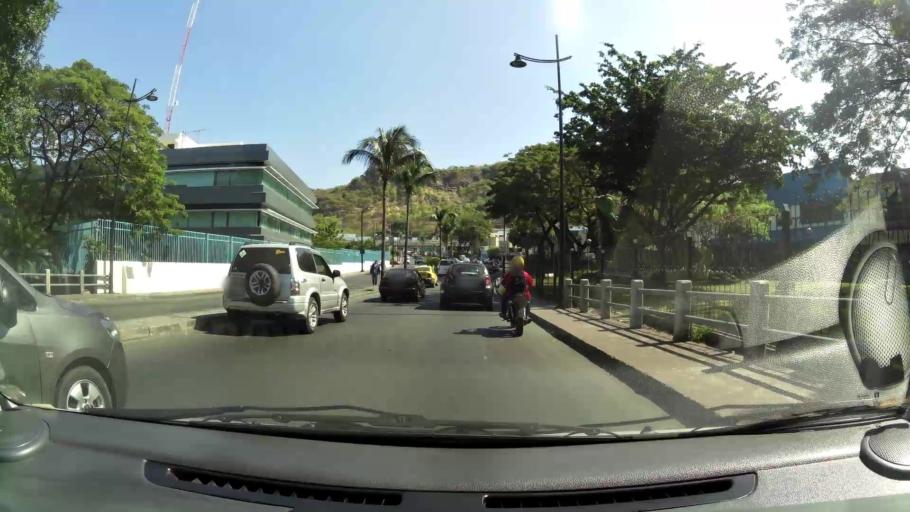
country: EC
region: Guayas
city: Guayaquil
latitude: -2.1725
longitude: -79.9131
